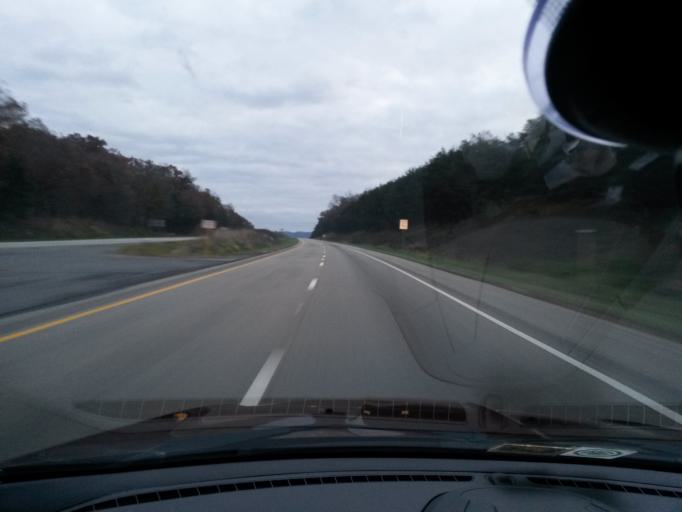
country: US
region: Virginia
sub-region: Alleghany County
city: Clifton Forge
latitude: 37.8270
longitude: -79.7831
